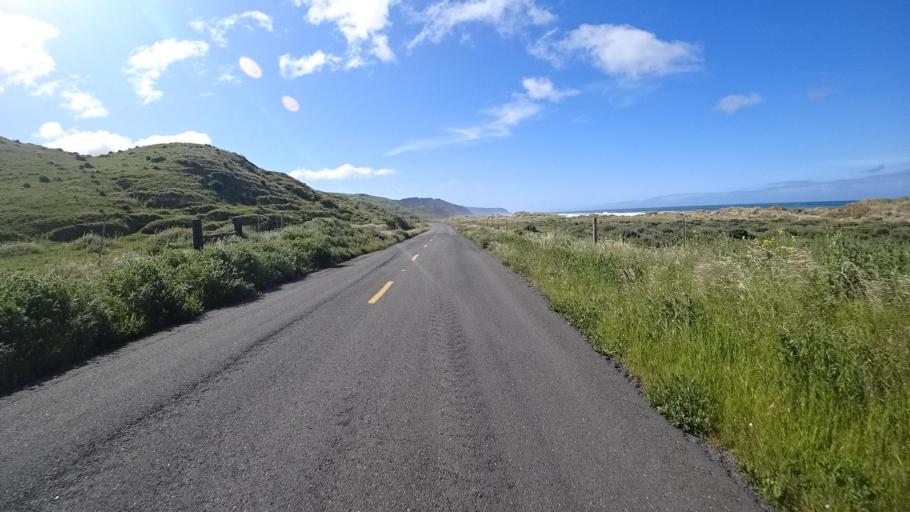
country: US
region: California
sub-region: Humboldt County
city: Ferndale
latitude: 40.3821
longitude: -124.3667
